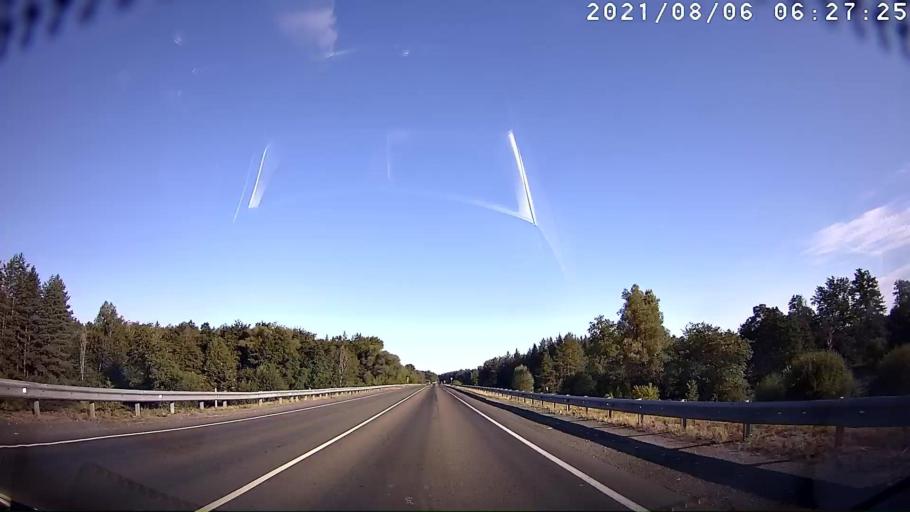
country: RU
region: Mariy-El
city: Krasnogorskiy
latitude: 56.1347
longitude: 48.3283
